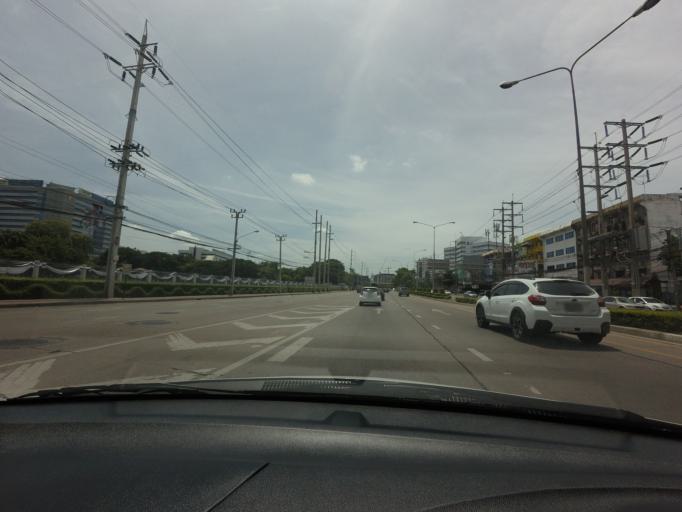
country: TH
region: Bangkok
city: Lak Si
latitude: 13.8864
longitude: 100.5779
